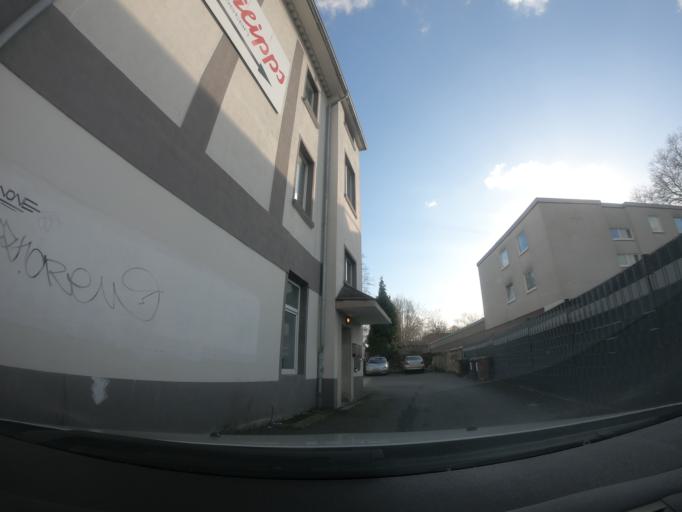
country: DE
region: North Rhine-Westphalia
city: Lunen
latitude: 51.5694
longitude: 7.5188
